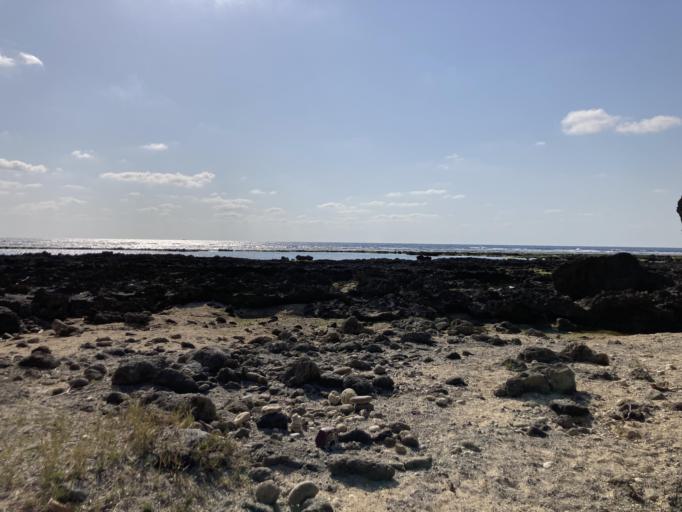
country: JP
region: Okinawa
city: Itoman
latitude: 26.1175
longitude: 127.7465
